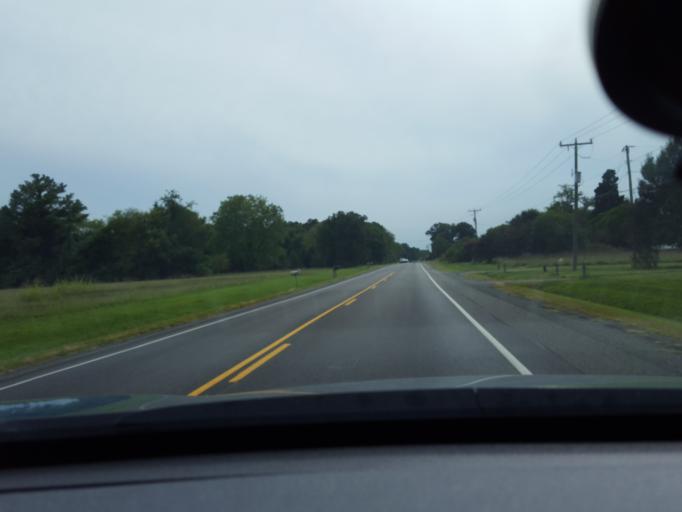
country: US
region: Virginia
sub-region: Hanover County
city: Hanover
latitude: 37.7304
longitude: -77.3619
